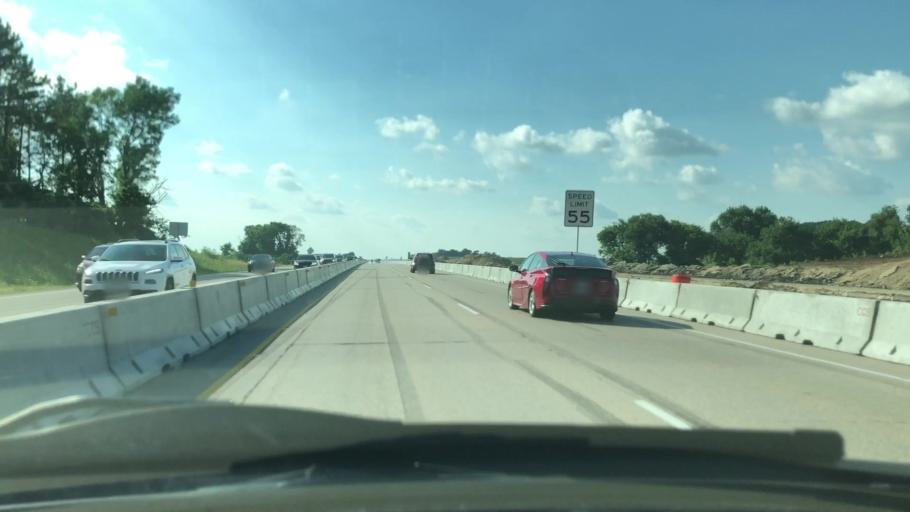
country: US
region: Wisconsin
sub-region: Dane County
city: Deerfield
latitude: 42.9687
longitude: -89.1082
